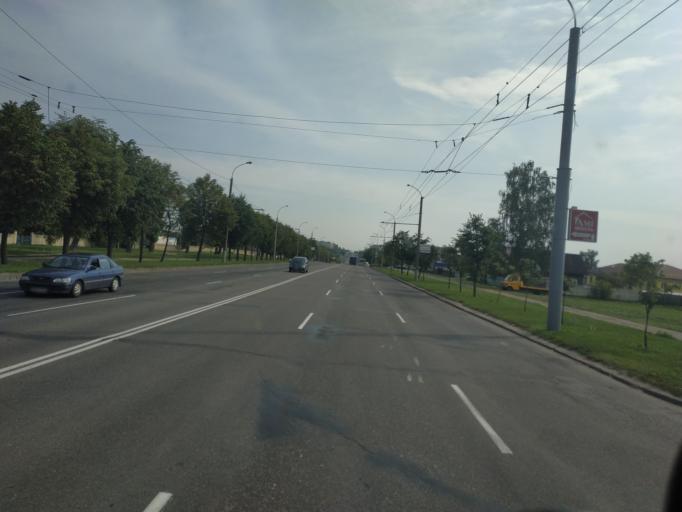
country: BY
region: Mogilev
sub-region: Mahilyowski Rayon
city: Veyno
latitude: 53.8671
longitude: 30.3631
